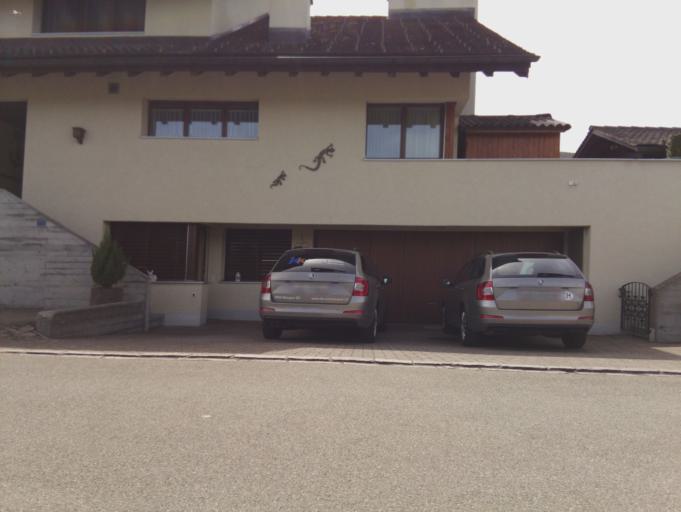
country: CH
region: Schwyz
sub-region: Bezirk March
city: Lachen
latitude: 47.1796
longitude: 8.8663
